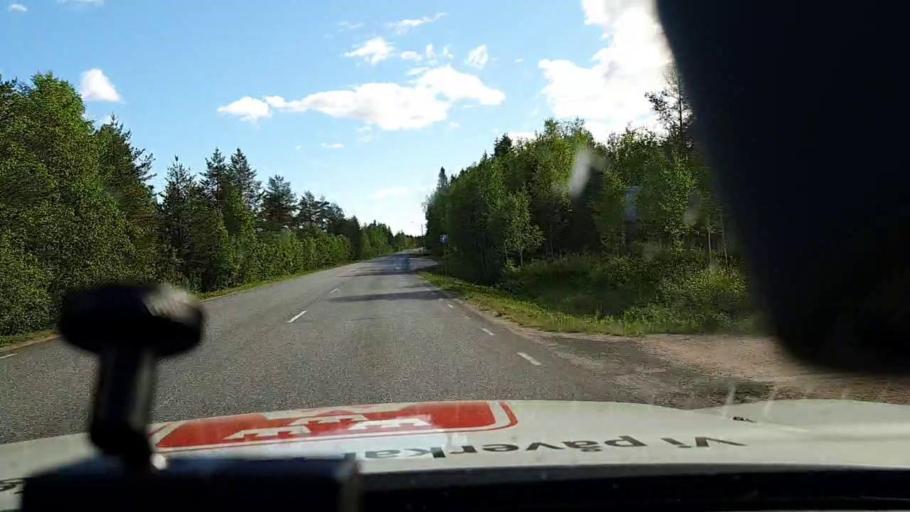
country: FI
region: Lapland
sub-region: Torniolaakso
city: Ylitornio
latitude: 66.3420
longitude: 23.6473
